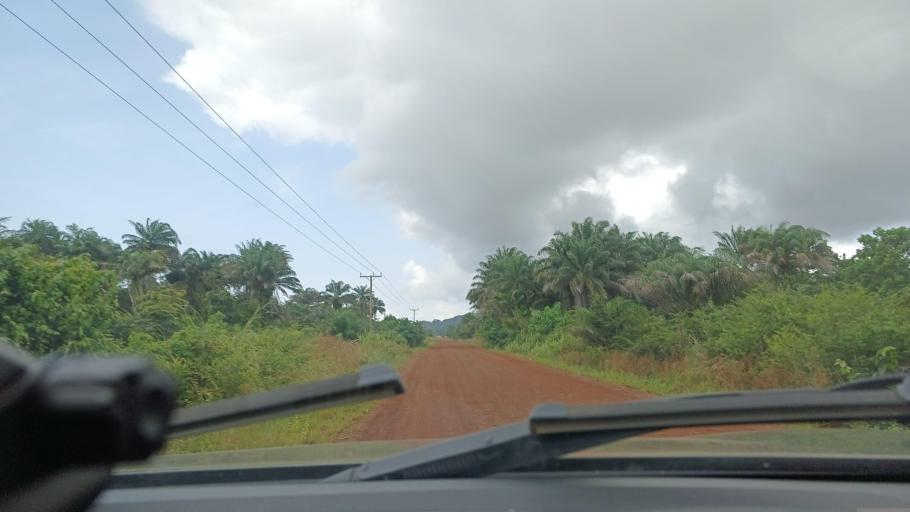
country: LR
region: Grand Cape Mount
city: Robertsport
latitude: 6.7032
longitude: -11.3214
